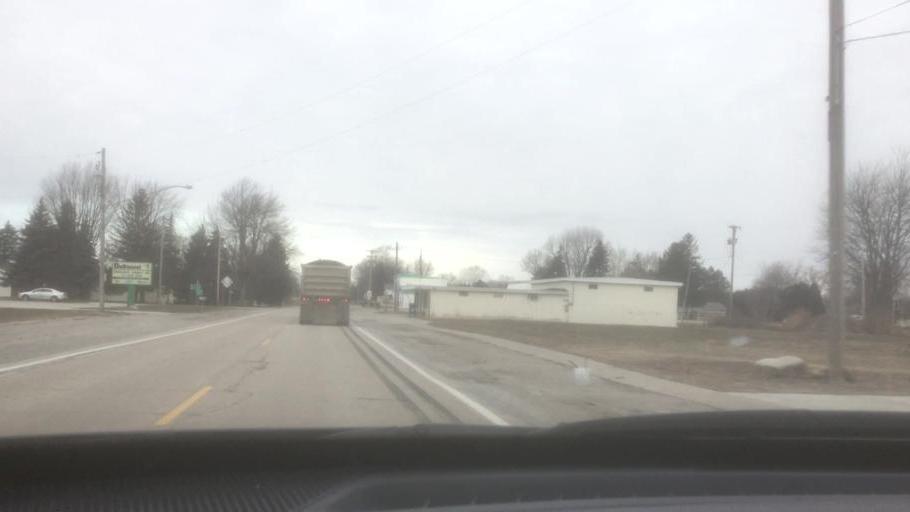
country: US
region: Michigan
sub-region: Tuscola County
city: Reese
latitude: 43.5220
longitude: -83.7770
